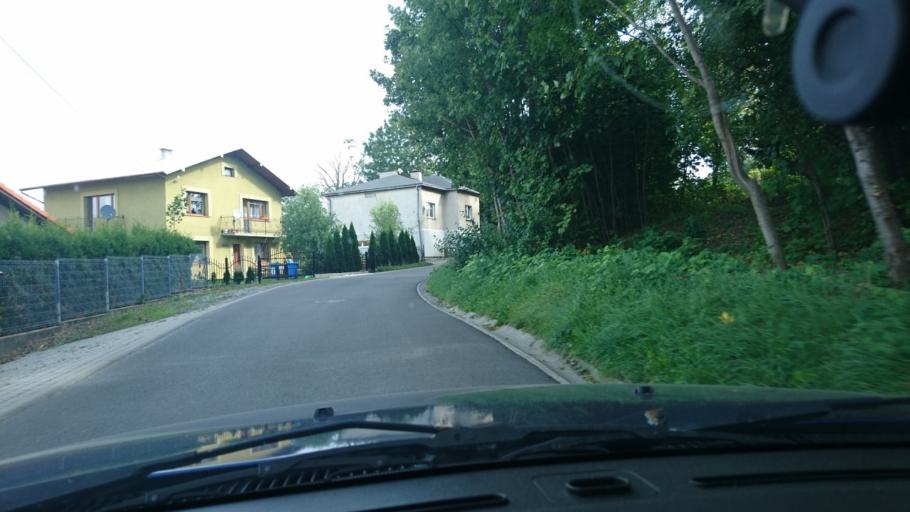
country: PL
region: Silesian Voivodeship
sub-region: Powiat bielski
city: Mazancowice
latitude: 49.8186
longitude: 18.9912
